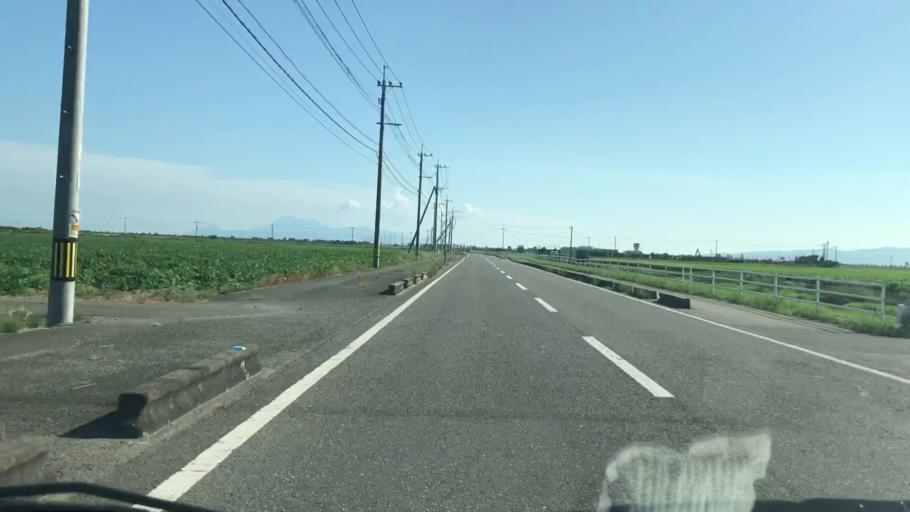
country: JP
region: Saga Prefecture
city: Okawa
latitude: 33.1685
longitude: 130.3098
